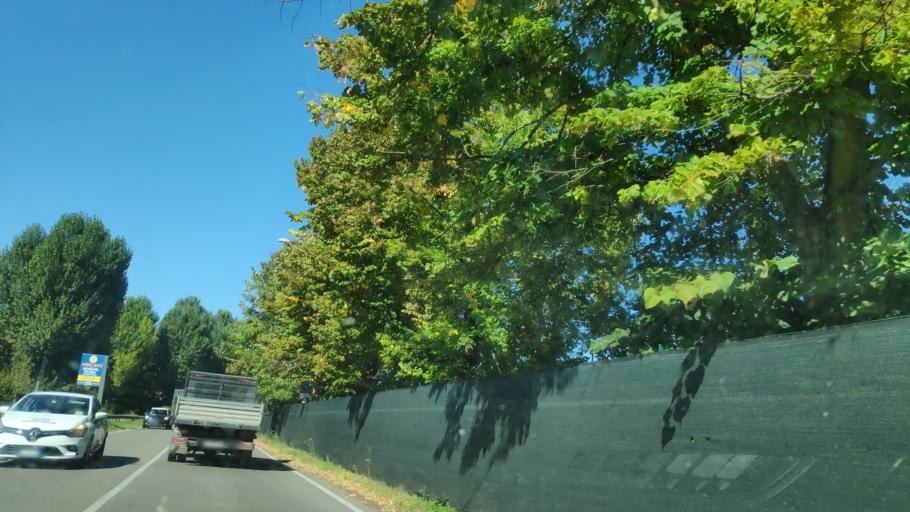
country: IT
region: Lombardy
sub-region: Citta metropolitana di Milano
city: Basiglio
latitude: 45.3679
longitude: 9.1685
